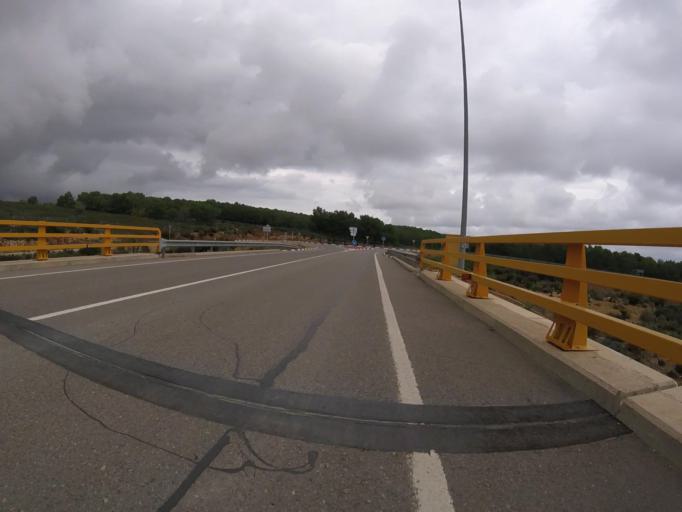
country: ES
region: Valencia
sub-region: Provincia de Castello
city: Benlloch
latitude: 40.2159
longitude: 0.0954
